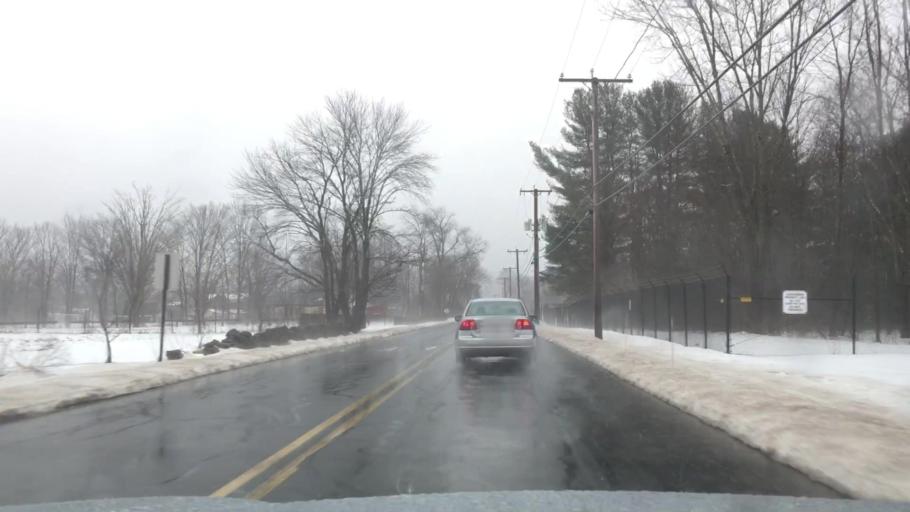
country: US
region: Massachusetts
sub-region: Hampshire County
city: Granby
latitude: 42.2261
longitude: -72.4946
